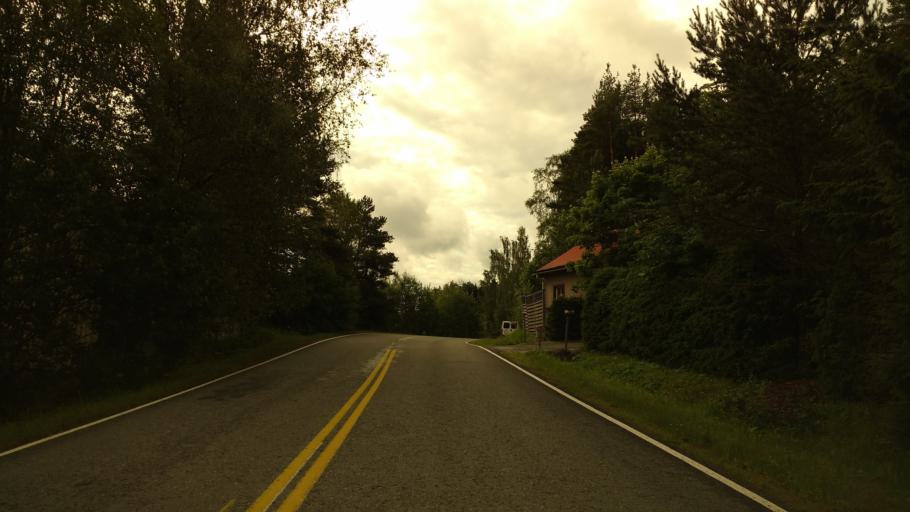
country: FI
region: Varsinais-Suomi
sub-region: Salo
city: Kuusjoki
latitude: 60.5255
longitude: 23.1735
